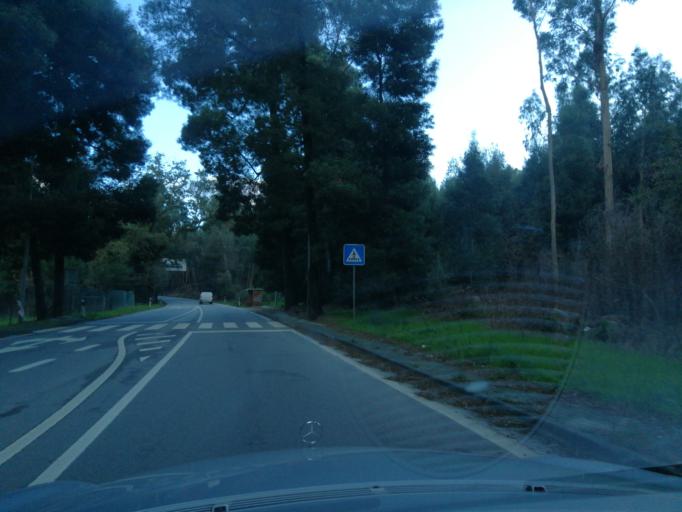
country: PT
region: Braga
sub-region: Esposende
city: Marinhas
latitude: 41.5836
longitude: -8.7337
